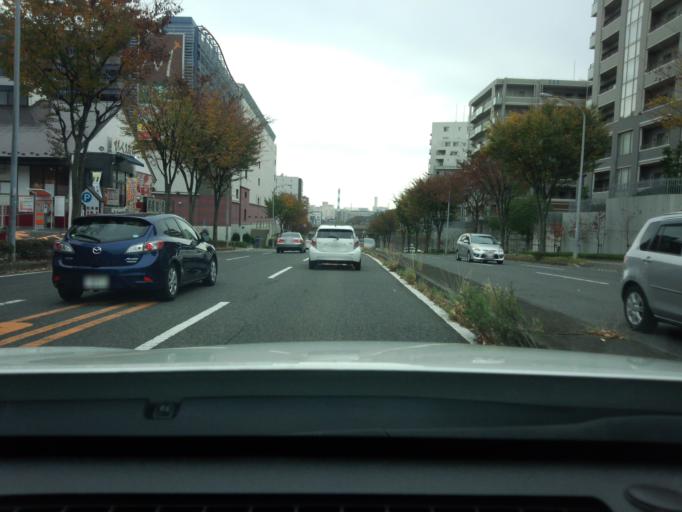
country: JP
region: Tokyo
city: Chofugaoka
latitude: 35.5564
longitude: 139.5776
